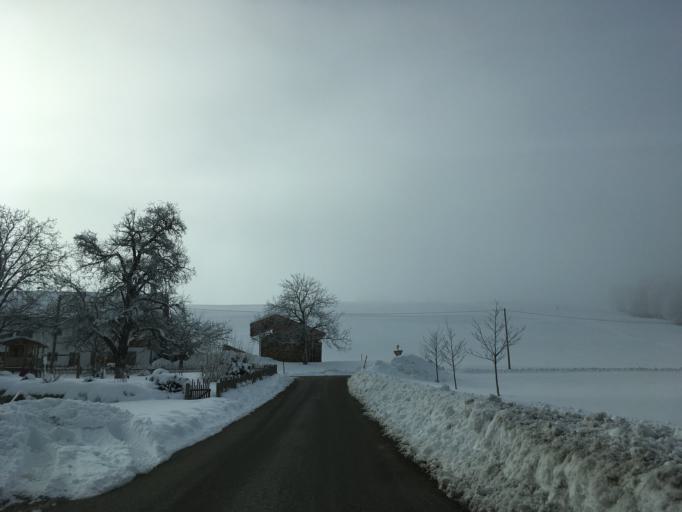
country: DE
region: Bavaria
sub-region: Upper Bavaria
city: Frasdorf
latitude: 47.8446
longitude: 12.2754
